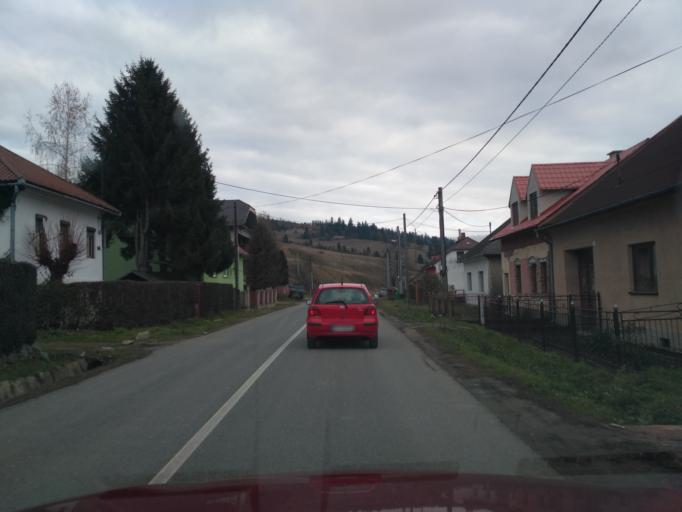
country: SK
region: Kosicky
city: Krompachy
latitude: 48.8115
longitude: 20.7178
